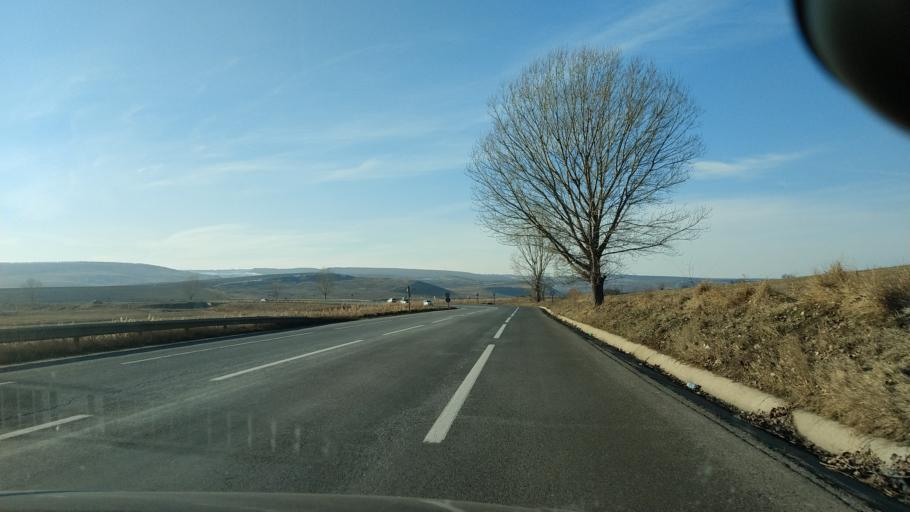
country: RO
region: Iasi
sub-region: Comuna Targu Frumos
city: Targu Frumos
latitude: 47.1981
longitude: 26.9789
